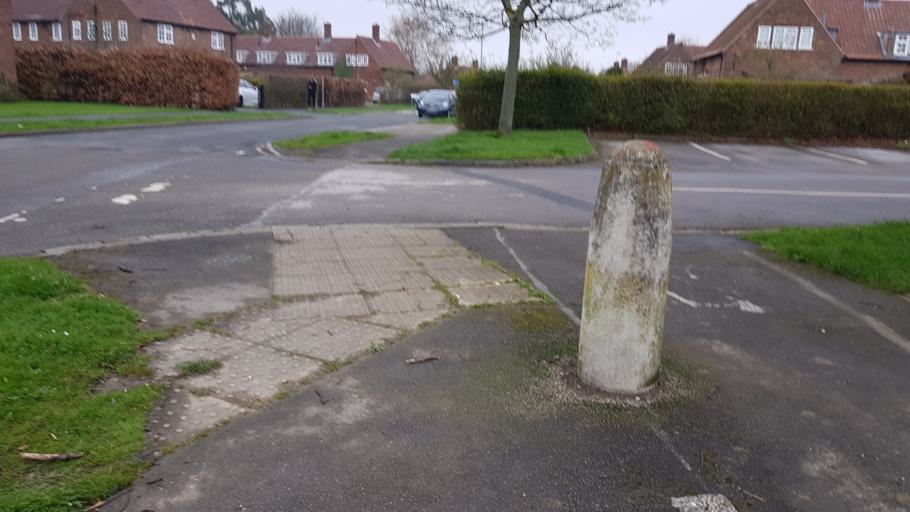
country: GB
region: England
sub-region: City of York
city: Haxby
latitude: 53.9882
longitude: -1.0769
